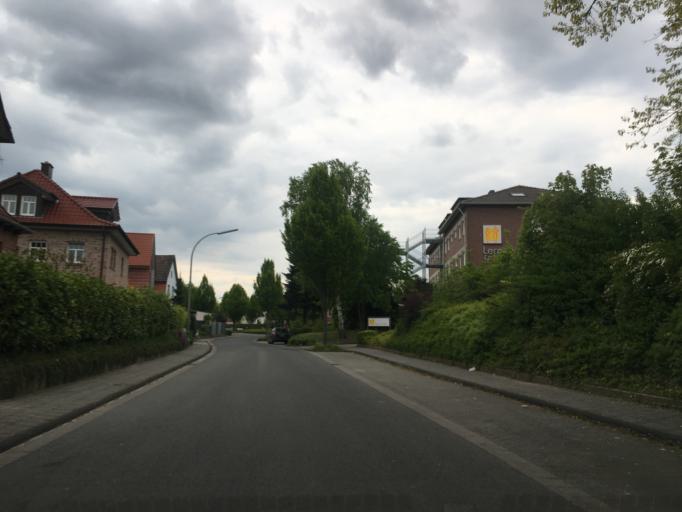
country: DE
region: North Rhine-Westphalia
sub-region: Regierungsbezirk Munster
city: Steinfurt
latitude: 52.1525
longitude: 7.3488
